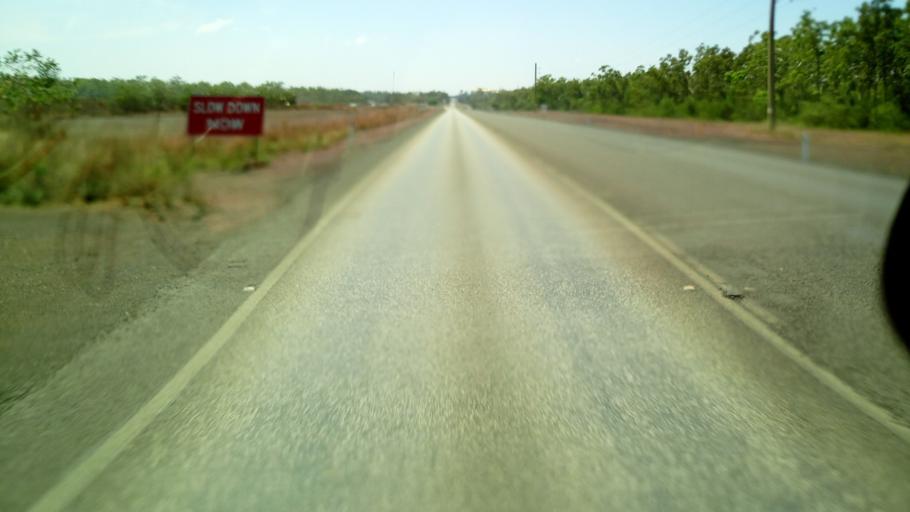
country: AU
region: Northern Territory
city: Alyangula
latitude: -13.9669
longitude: 136.4428
